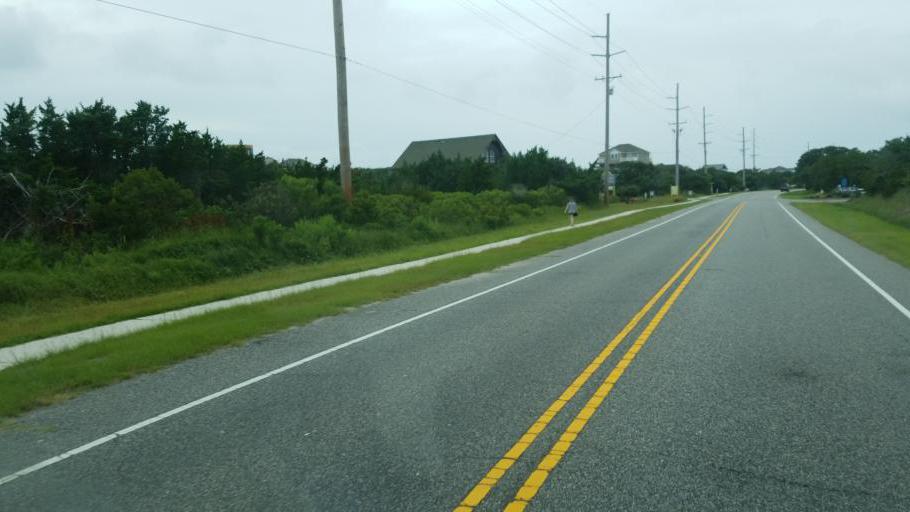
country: US
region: North Carolina
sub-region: Dare County
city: Buxton
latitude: 35.5357
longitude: -75.4732
